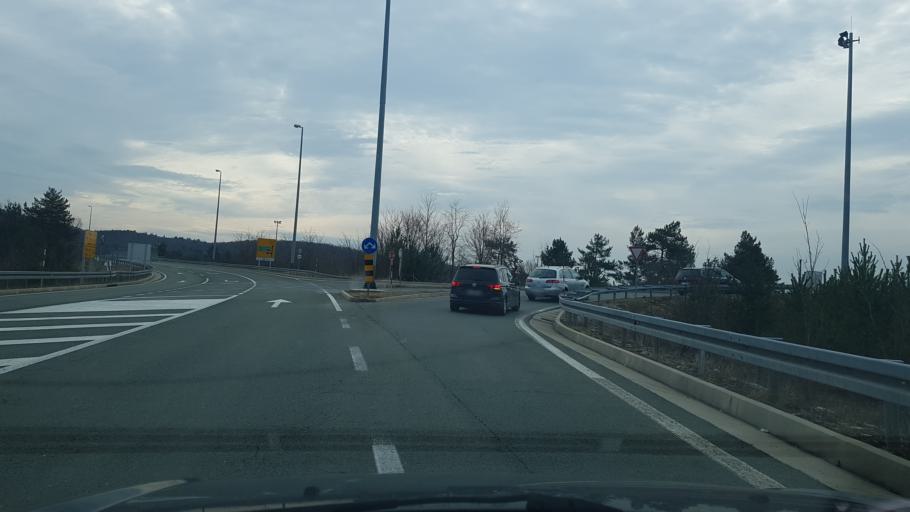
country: HR
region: Primorsko-Goranska
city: Klana
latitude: 45.4748
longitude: 14.2736
